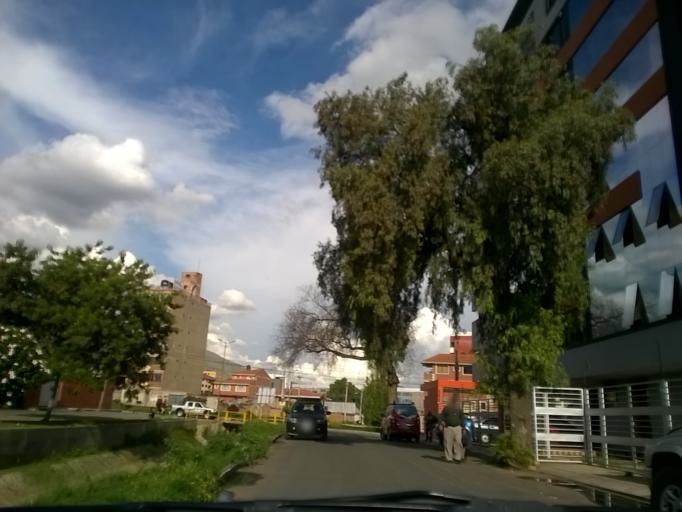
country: BO
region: Cochabamba
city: Cochabamba
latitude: -17.3657
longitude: -66.1796
